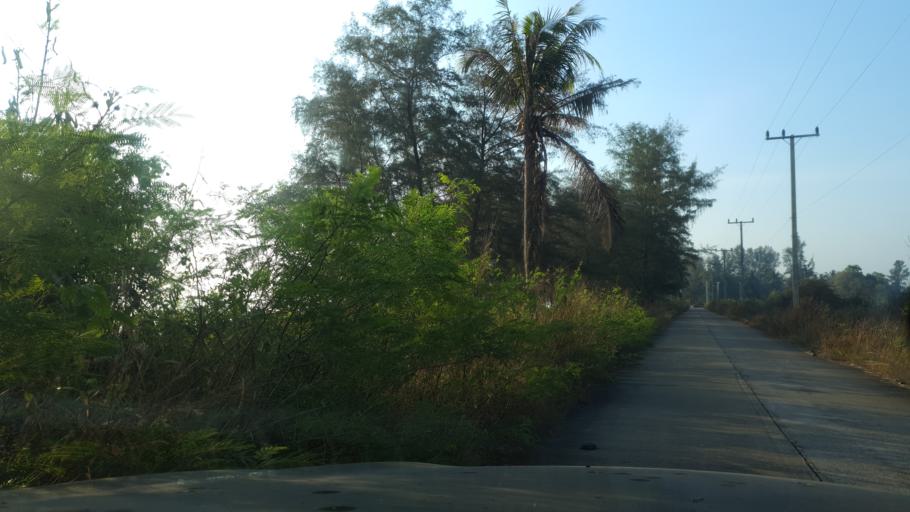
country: TH
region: Prachuap Khiri Khan
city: Bang Saphan
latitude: 11.3075
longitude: 99.5519
